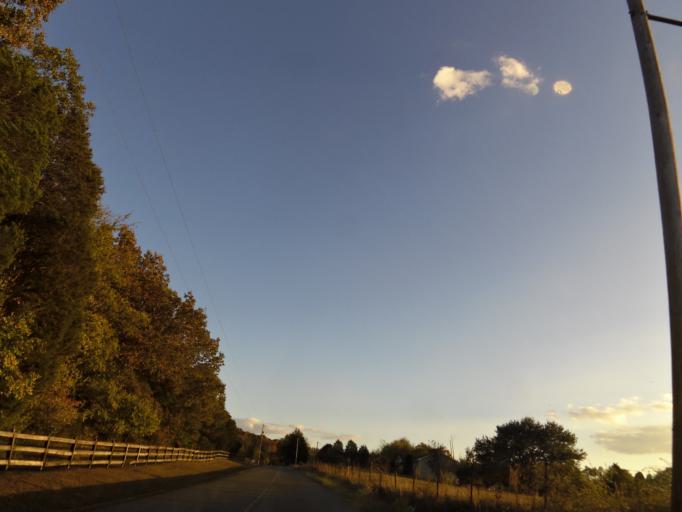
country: US
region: Tennessee
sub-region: Sevier County
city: Seymour
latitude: 35.9455
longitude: -83.7239
